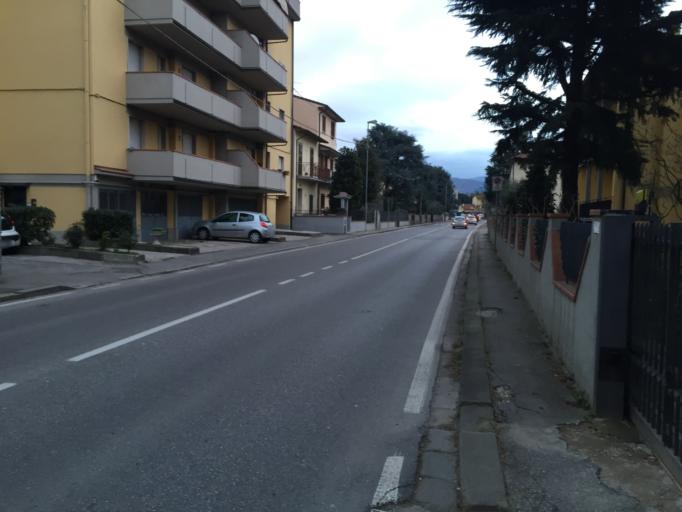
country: IT
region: Tuscany
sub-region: Provincia di Prato
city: Fornacelle
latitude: 43.8855
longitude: 11.0449
